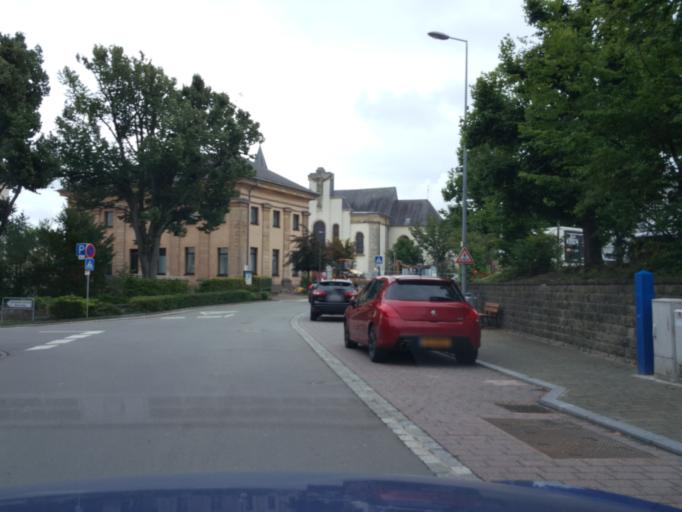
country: LU
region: Luxembourg
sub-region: Canton de Capellen
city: Mamer
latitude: 49.6273
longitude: 6.0217
